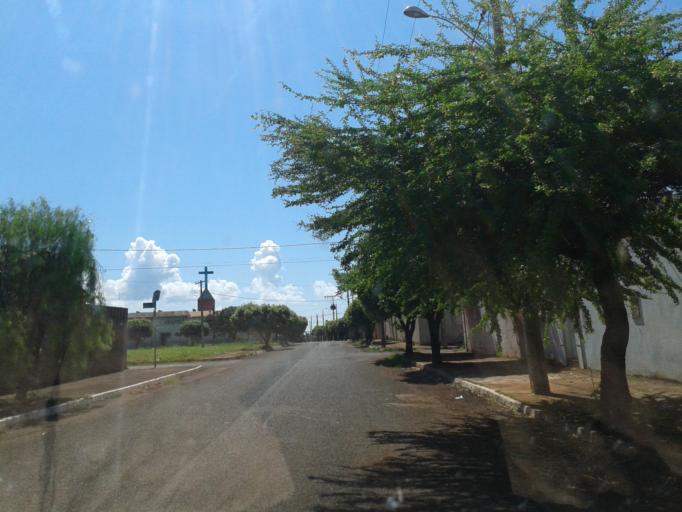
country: BR
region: Goias
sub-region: Itumbiara
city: Itumbiara
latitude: -18.4302
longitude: -49.1899
